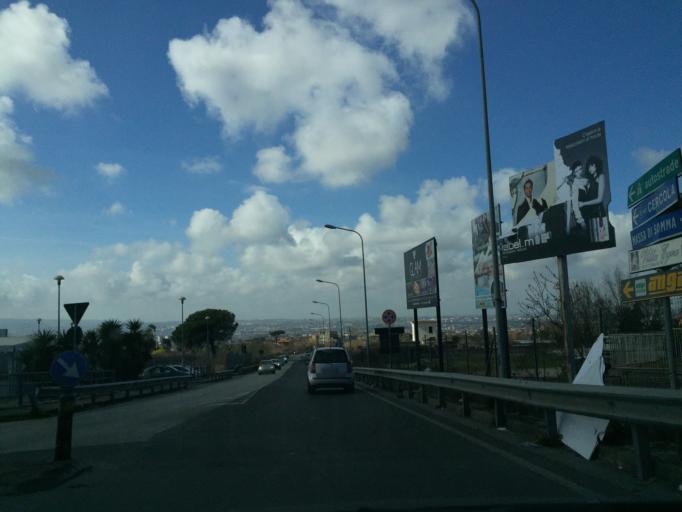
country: IT
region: Campania
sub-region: Provincia di Napoli
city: Pollena Trocchia
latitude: 40.8515
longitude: 14.3741
